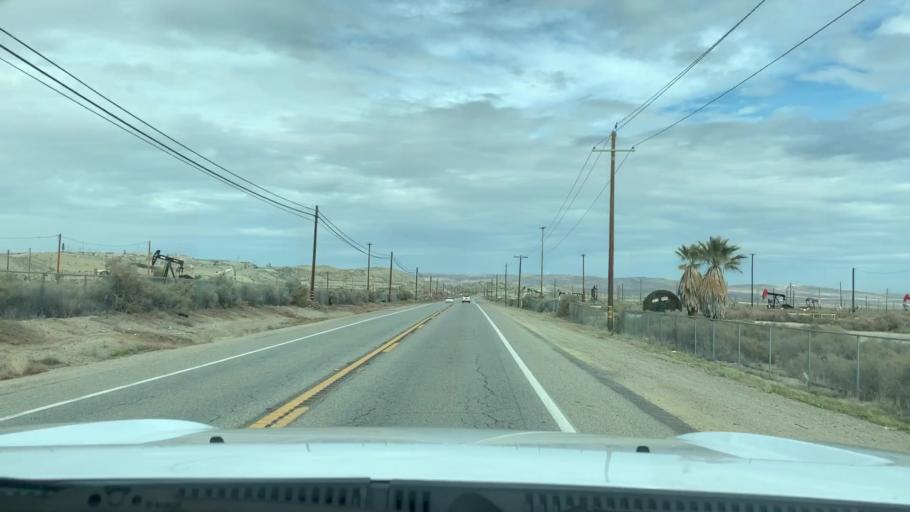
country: US
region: California
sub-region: Kern County
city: Maricopa
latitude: 35.0678
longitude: -119.4020
